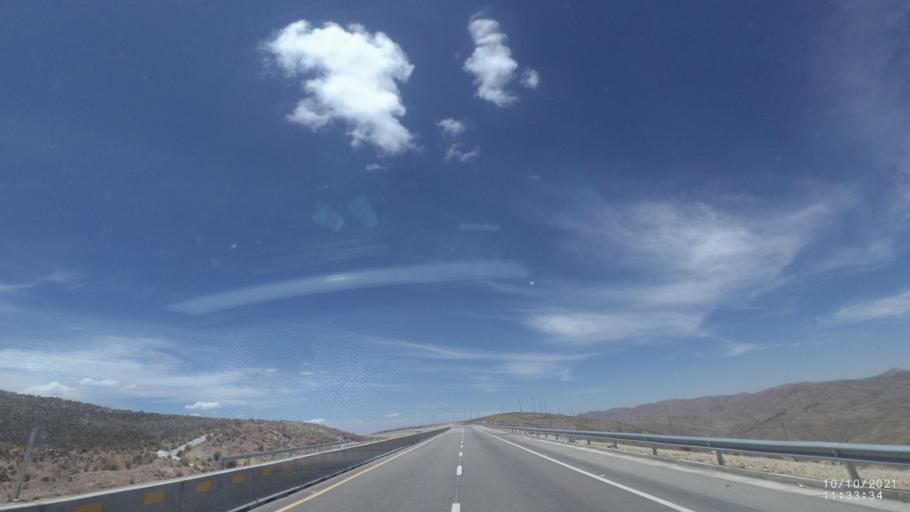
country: BO
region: Cochabamba
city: Colchani
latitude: -17.6449
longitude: -66.8446
